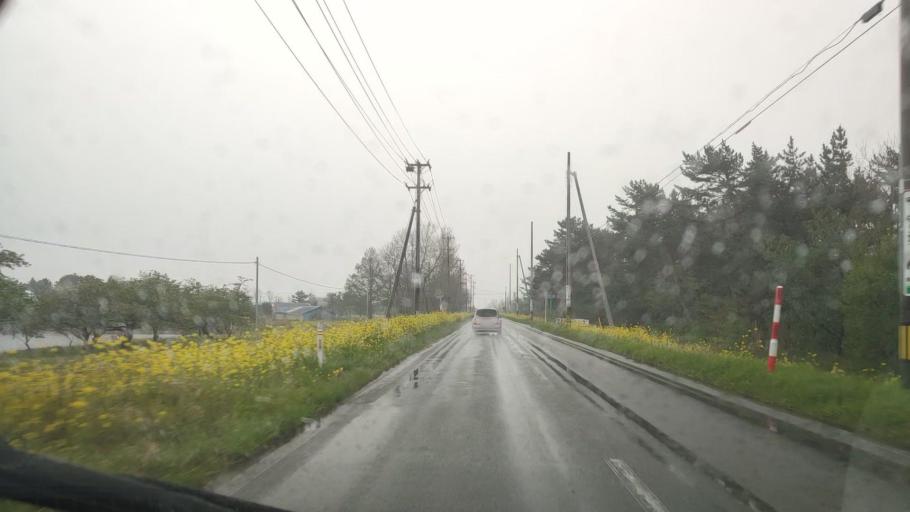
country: JP
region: Akita
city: Tenno
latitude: 40.0037
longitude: 139.9480
